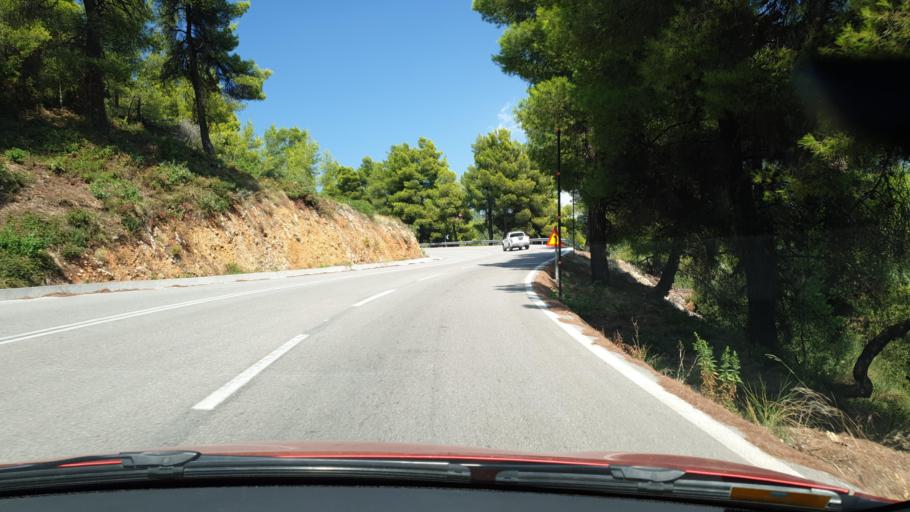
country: GR
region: Central Greece
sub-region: Nomos Evvoias
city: Politika
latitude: 38.6352
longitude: 23.5685
